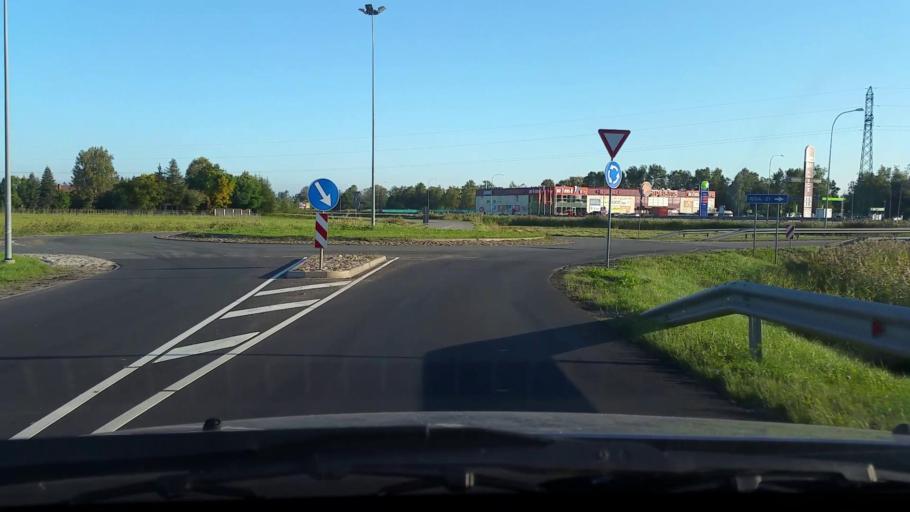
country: LV
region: Adazi
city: Adazi
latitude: 57.0694
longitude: 24.3180
